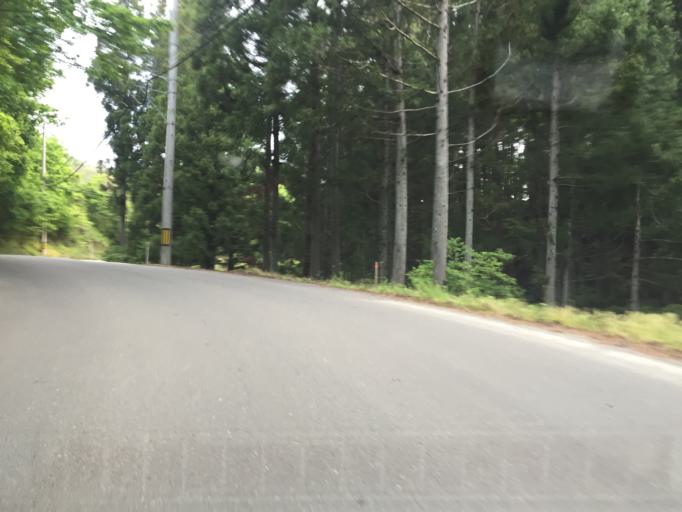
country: JP
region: Fukushima
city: Yanagawamachi-saiwaicho
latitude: 37.8951
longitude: 140.6703
